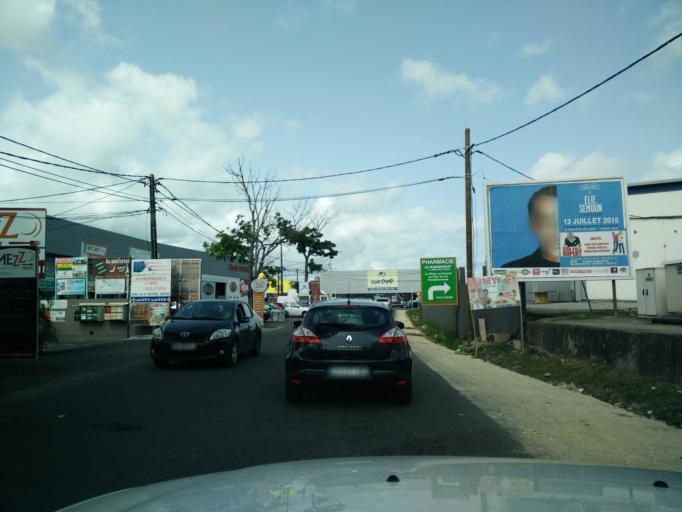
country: GP
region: Guadeloupe
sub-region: Guadeloupe
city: Pointe-a-Pitre
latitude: 16.2437
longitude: -61.5608
